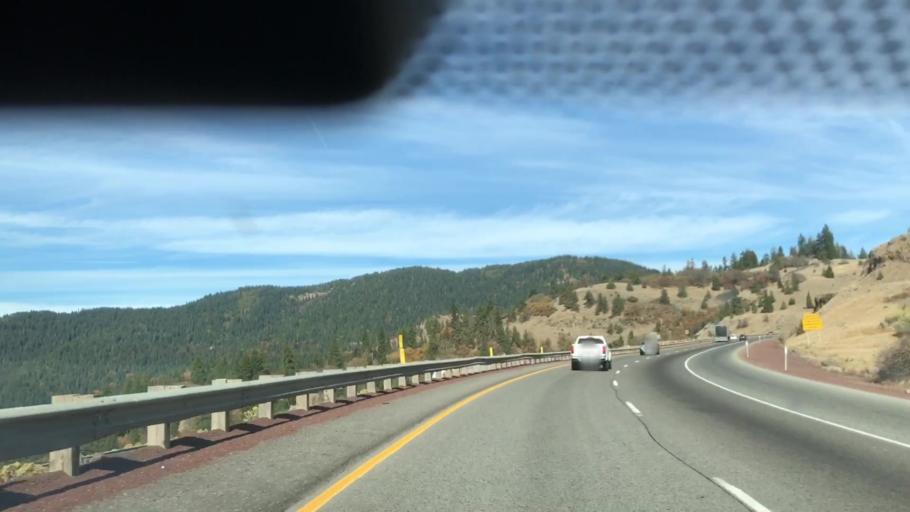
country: US
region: Oregon
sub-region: Jackson County
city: Ashland
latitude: 42.0534
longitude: -122.6100
